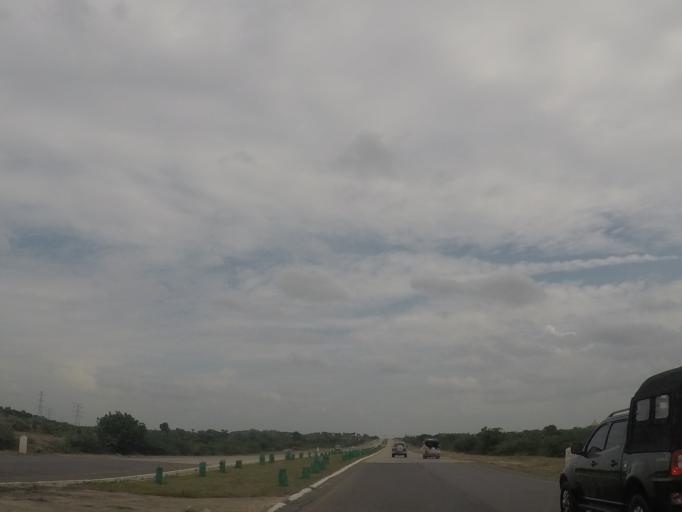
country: MM
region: Sagain
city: Sagaing
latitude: 21.7456
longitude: 95.9794
